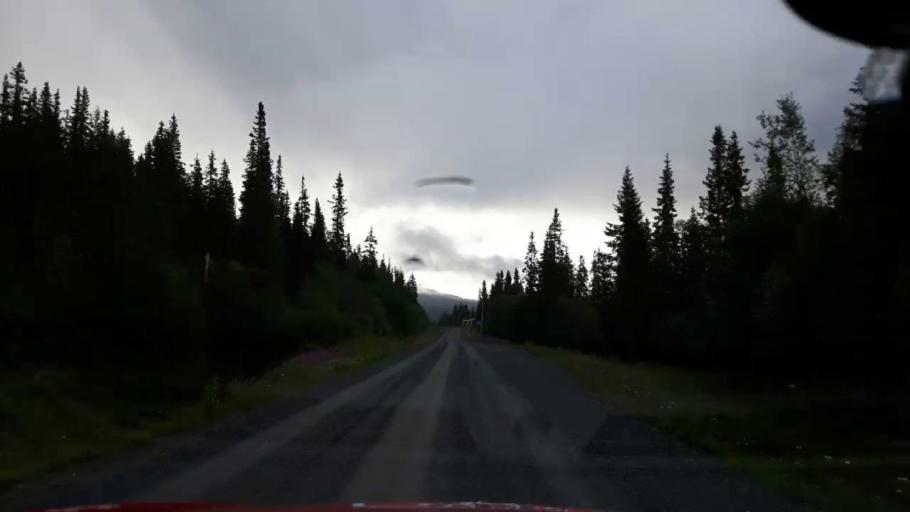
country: NO
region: Nordland
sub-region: Hattfjelldal
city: Hattfjelldal
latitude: 64.8827
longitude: 14.7807
